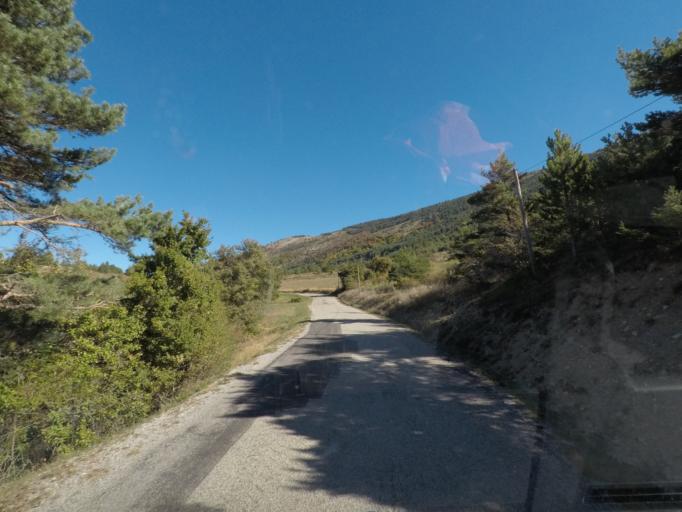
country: FR
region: Rhone-Alpes
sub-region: Departement de la Drome
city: Die
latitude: 44.5374
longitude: 5.3684
